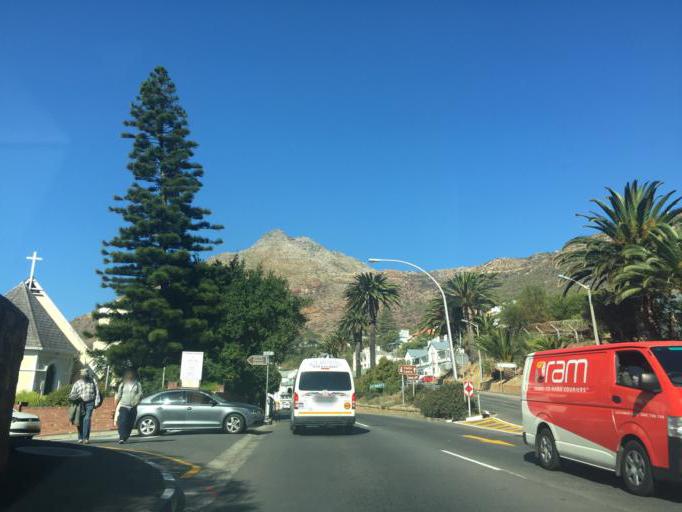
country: ZA
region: Western Cape
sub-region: City of Cape Town
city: Retreat
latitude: -34.1891
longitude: 18.4259
